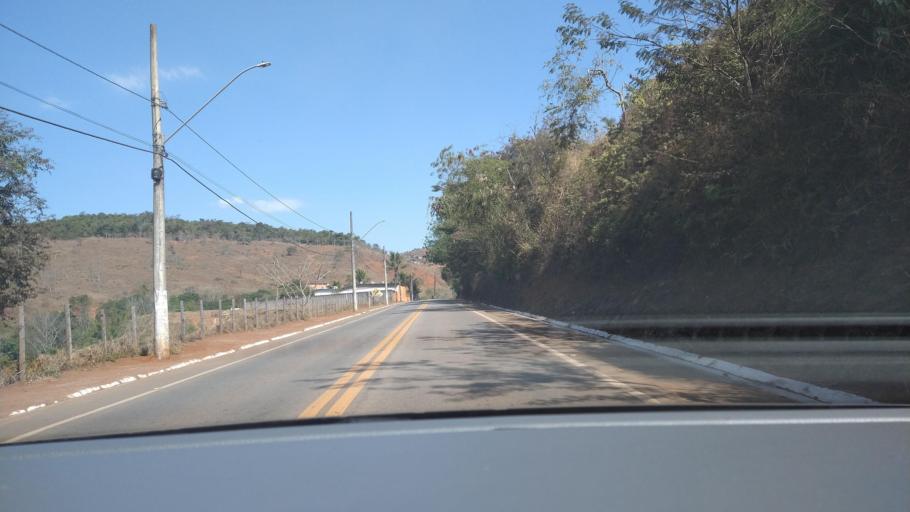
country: BR
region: Minas Gerais
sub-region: Rio Piracicaba
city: Rio Piracicaba
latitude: -19.9235
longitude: -43.1637
